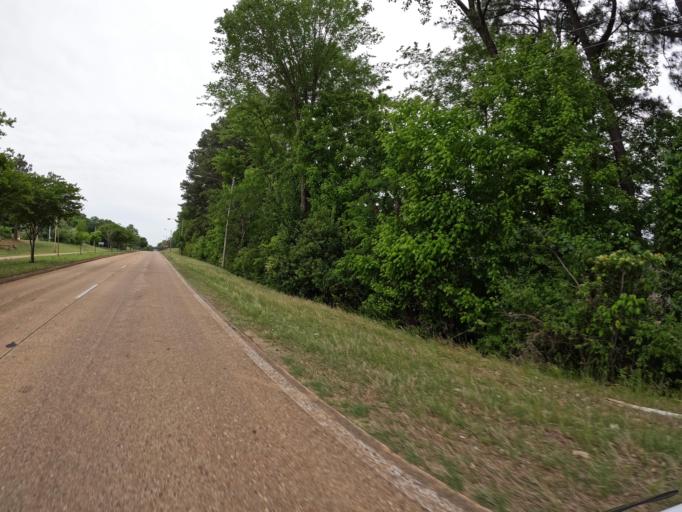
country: US
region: Mississippi
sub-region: Lee County
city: Tupelo
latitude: 34.2802
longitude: -88.7286
